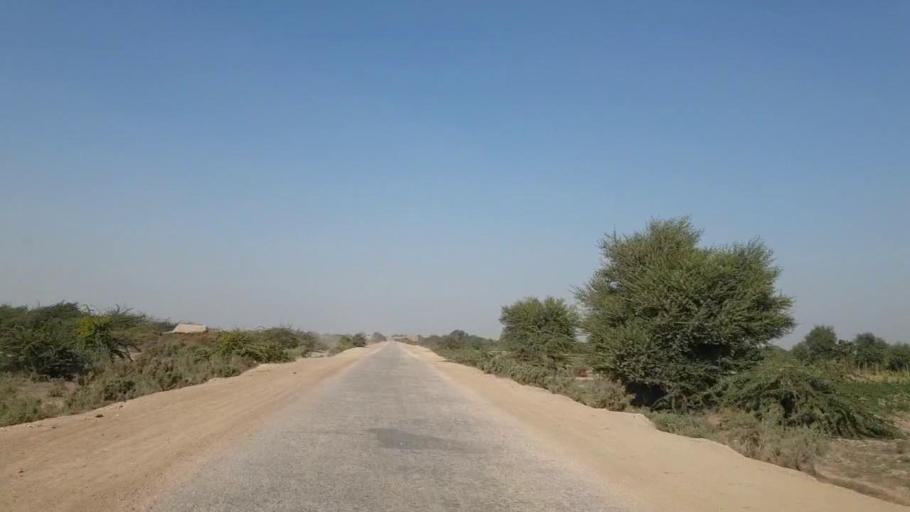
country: PK
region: Sindh
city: Digri
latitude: 25.0246
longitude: 69.1055
